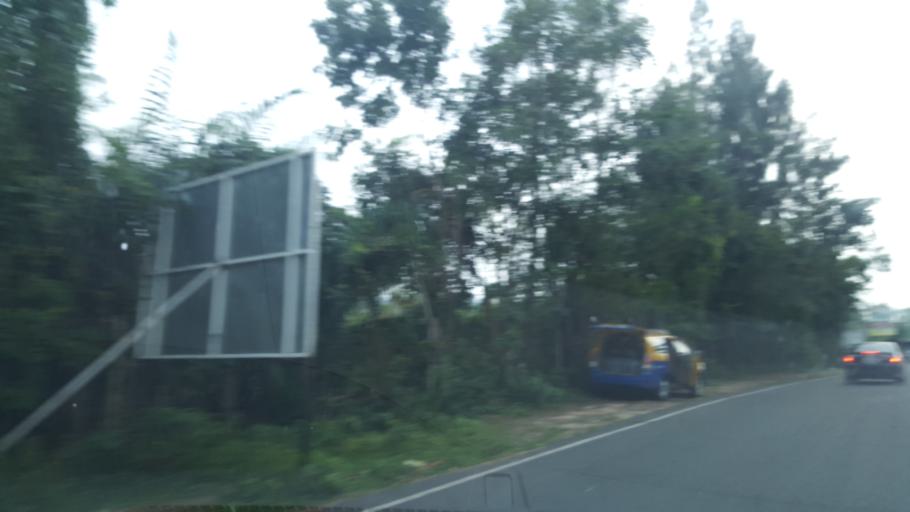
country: TH
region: Chon Buri
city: Ban Bueng
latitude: 13.2145
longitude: 101.0562
